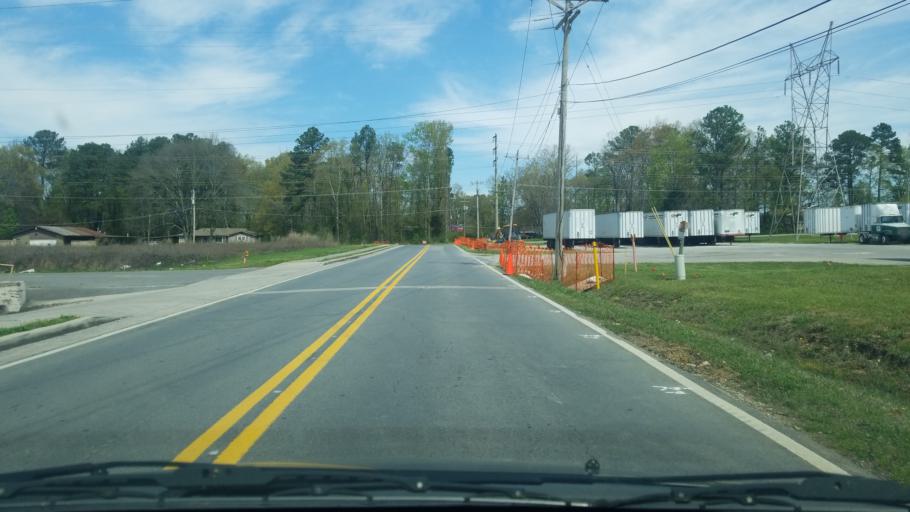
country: US
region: Georgia
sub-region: Catoosa County
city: Fort Oglethorpe
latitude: 34.9557
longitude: -85.2505
